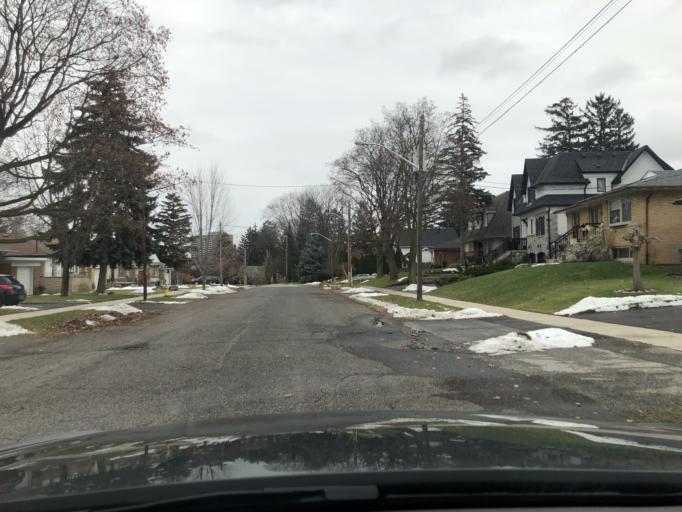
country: CA
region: Ontario
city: Etobicoke
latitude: 43.6949
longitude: -79.5236
